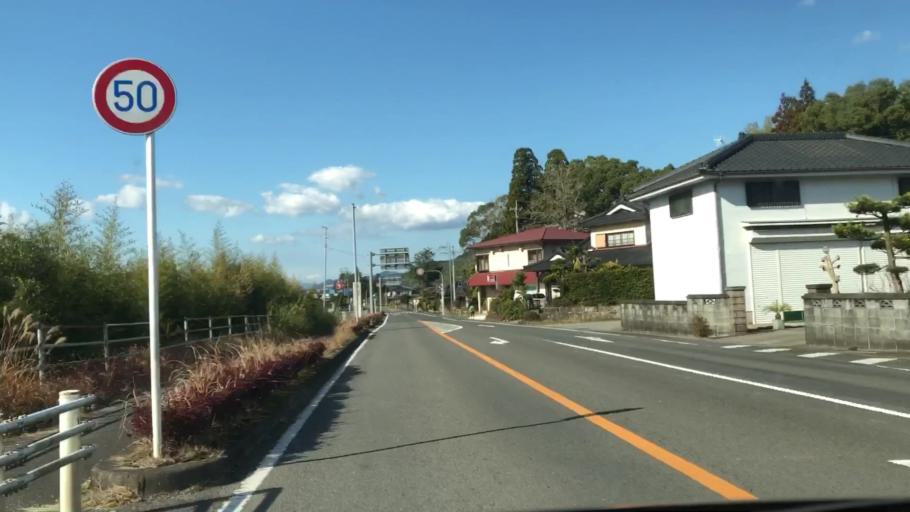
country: JP
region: Kagoshima
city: Satsumasendai
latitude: 31.7958
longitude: 130.4419
